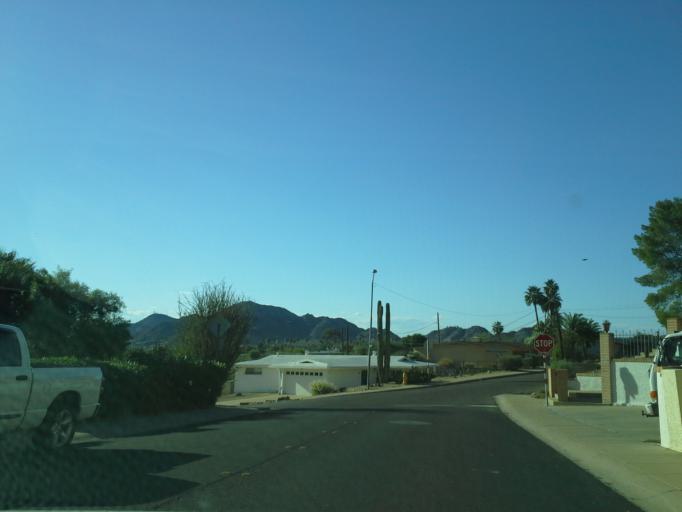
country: US
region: Arizona
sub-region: Maricopa County
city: Phoenix
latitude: 33.5603
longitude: -112.0530
